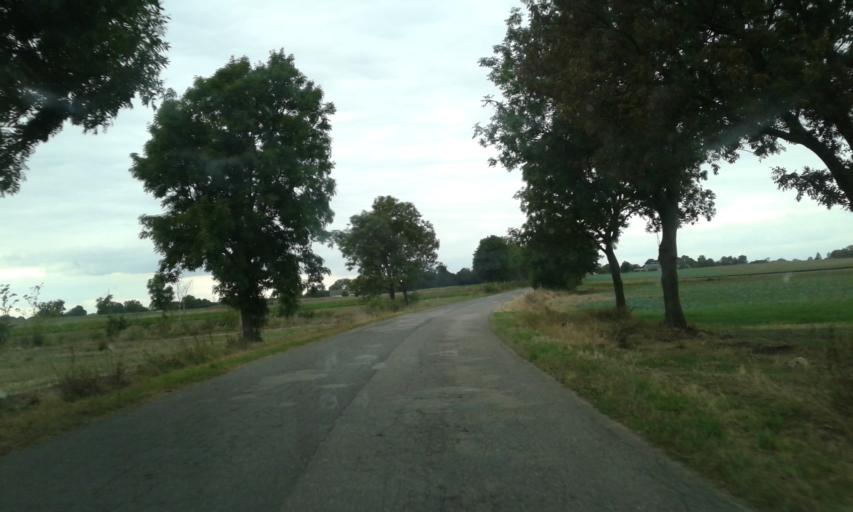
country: PL
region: West Pomeranian Voivodeship
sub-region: Powiat pyrzycki
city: Warnice
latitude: 53.1823
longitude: 15.0281
